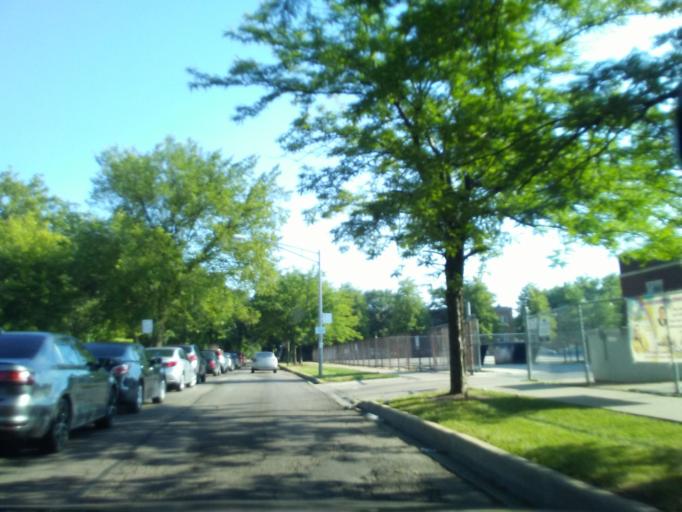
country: US
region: Illinois
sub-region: Cook County
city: Oak Park
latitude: 41.9326
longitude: -87.7405
